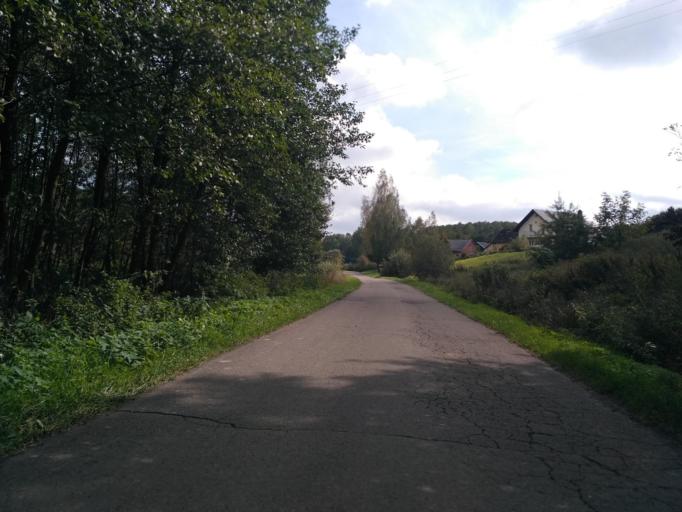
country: PL
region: Subcarpathian Voivodeship
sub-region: Powiat ropczycko-sedziszowski
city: Niedzwiada
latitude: 49.9363
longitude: 21.5315
